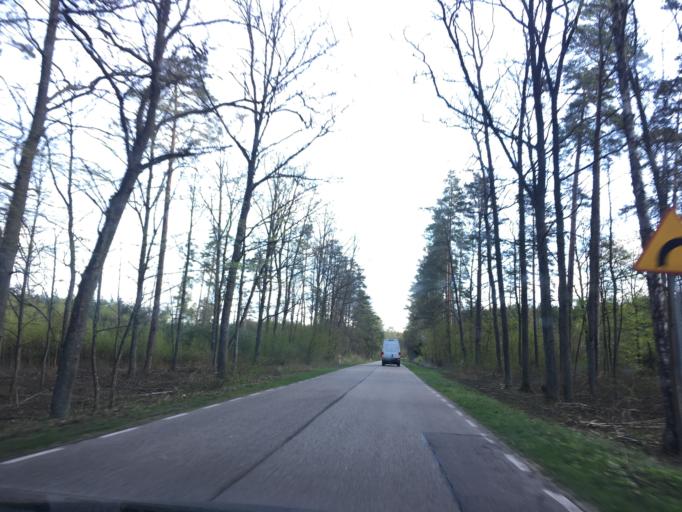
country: PL
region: Warmian-Masurian Voivodeship
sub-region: Powiat piski
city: Ruciane-Nida
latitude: 53.6702
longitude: 21.5754
